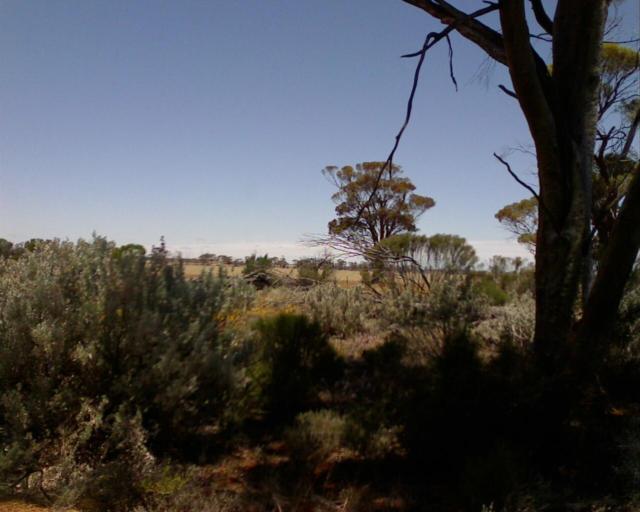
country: AU
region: Western Australia
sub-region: Merredin
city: Merredin
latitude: -30.9618
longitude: 118.8843
